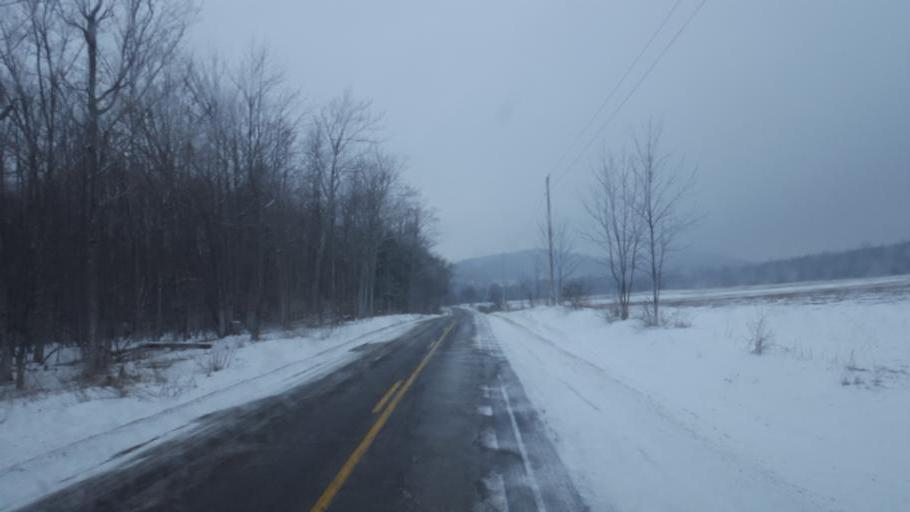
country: US
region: New York
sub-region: Steuben County
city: Canisteo
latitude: 42.1348
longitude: -77.5240
